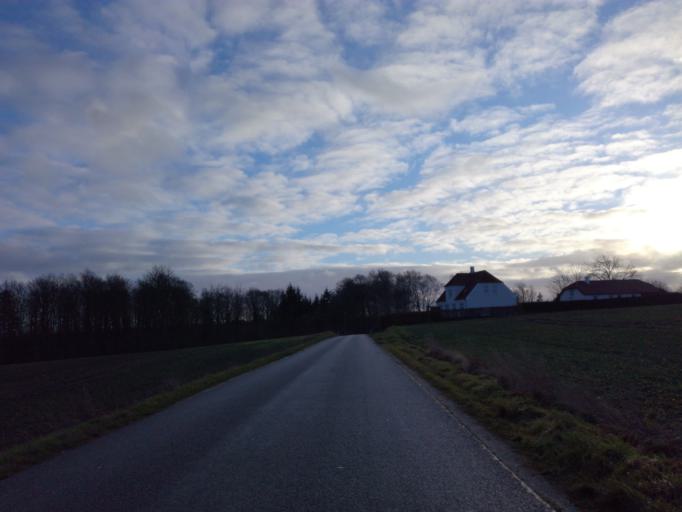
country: DK
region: South Denmark
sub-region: Fredericia Kommune
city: Taulov
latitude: 55.5539
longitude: 9.6025
